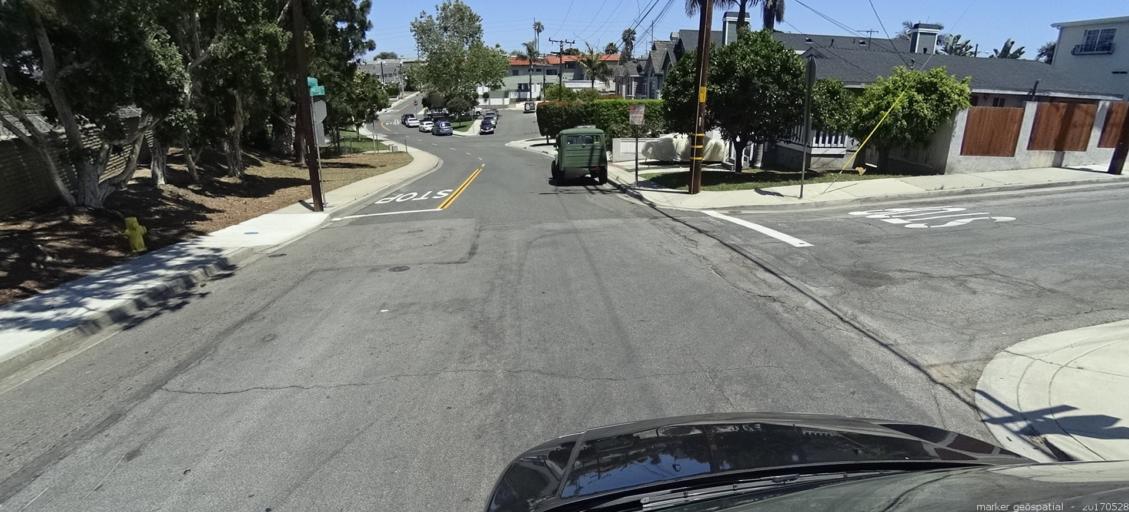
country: US
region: California
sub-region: Los Angeles County
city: Hermosa Beach
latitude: 33.8698
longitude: -118.3813
